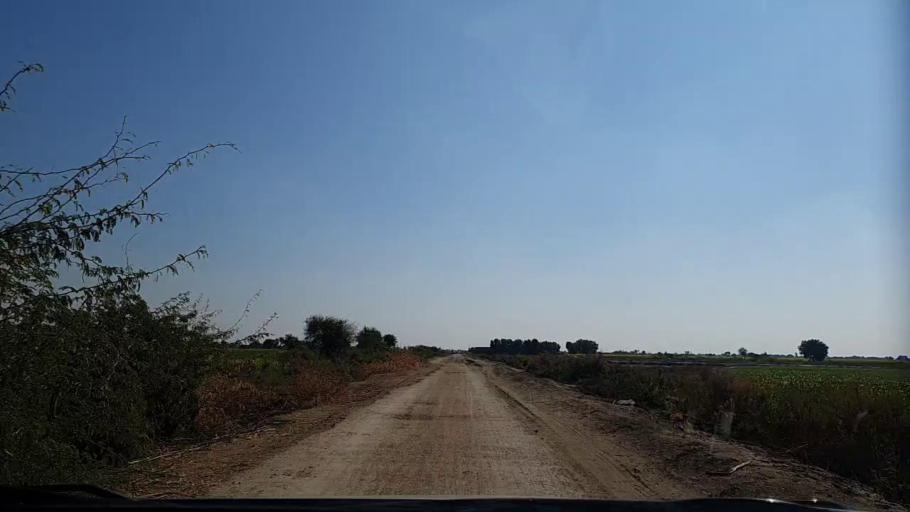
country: PK
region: Sindh
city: Pithoro
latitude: 25.7101
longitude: 69.3340
